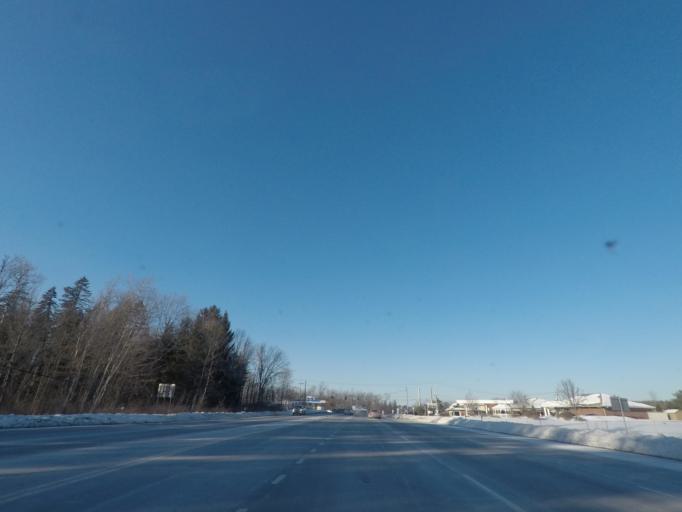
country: US
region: New York
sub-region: Saratoga County
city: Saratoga Springs
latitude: 43.0251
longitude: -73.7922
